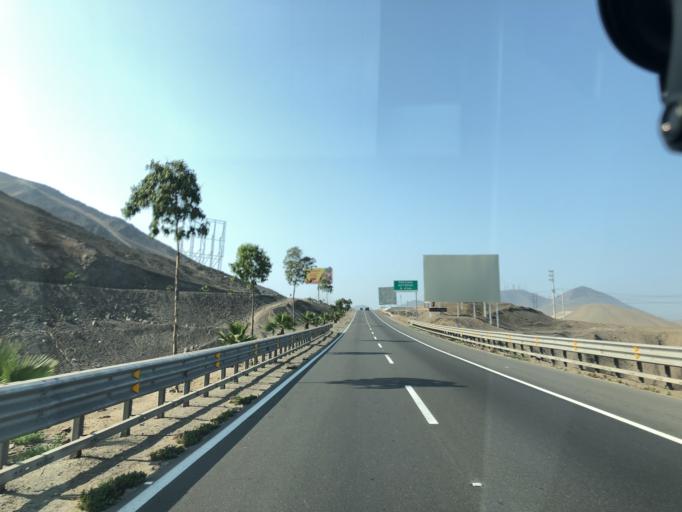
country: PE
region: Lima
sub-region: Lima
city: San Bartolo
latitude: -12.4316
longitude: -76.7539
